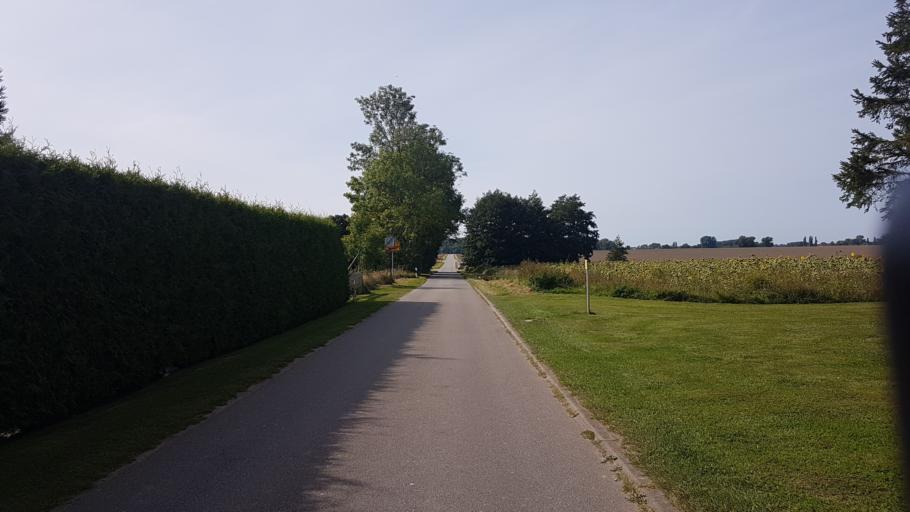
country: DE
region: Mecklenburg-Vorpommern
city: Gingst
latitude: 54.4199
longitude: 13.2492
